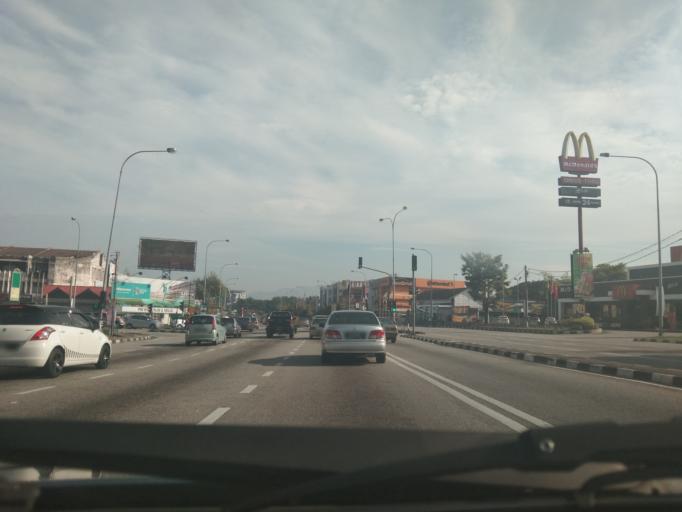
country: MY
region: Perak
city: Ipoh
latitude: 4.5718
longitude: 101.1125
